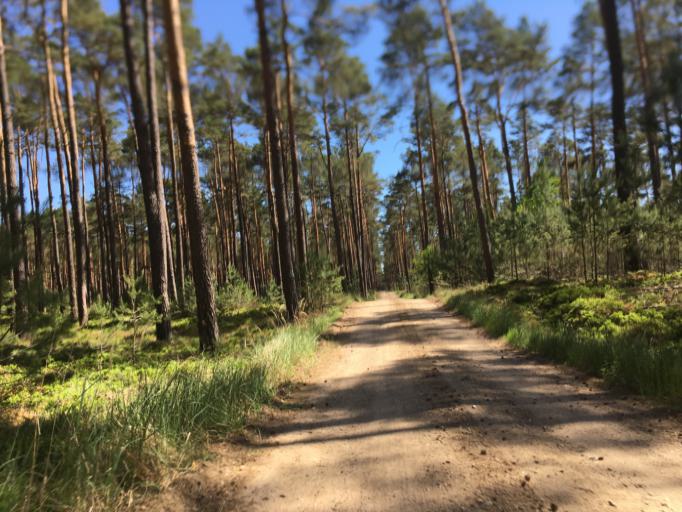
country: DE
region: Brandenburg
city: Friedrichswalde
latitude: 52.9686
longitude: 13.6360
